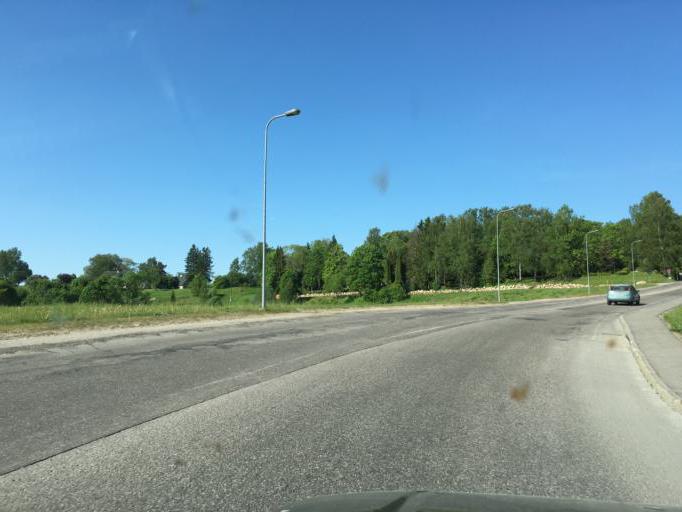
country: LV
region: Talsu Rajons
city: Talsi
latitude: 57.2388
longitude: 22.5989
